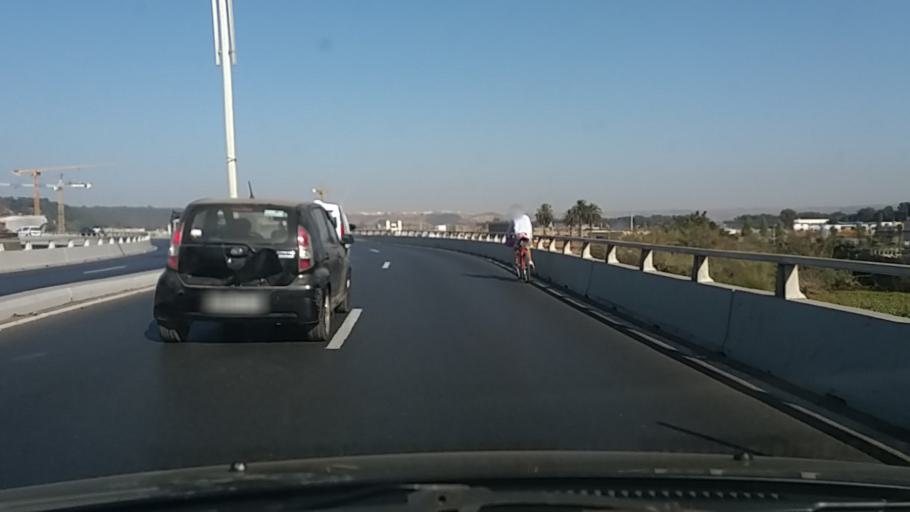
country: MA
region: Rabat-Sale-Zemmour-Zaer
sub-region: Rabat
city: Rabat
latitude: 34.0250
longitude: -6.8215
